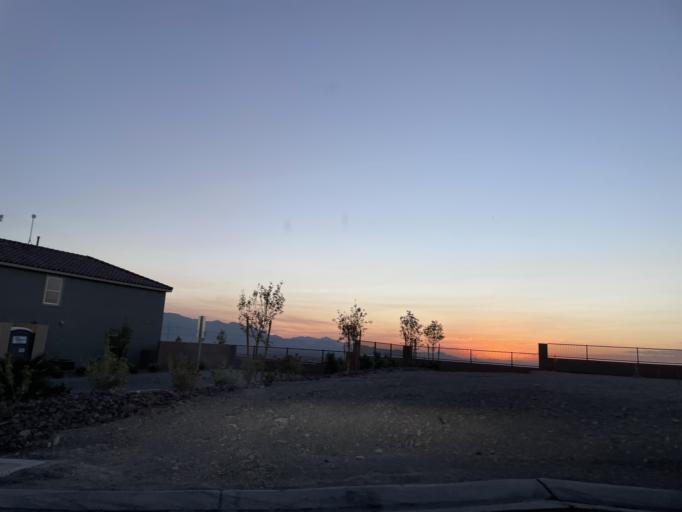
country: US
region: Nevada
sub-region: Clark County
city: Summerlin South
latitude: 36.2596
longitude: -115.3319
